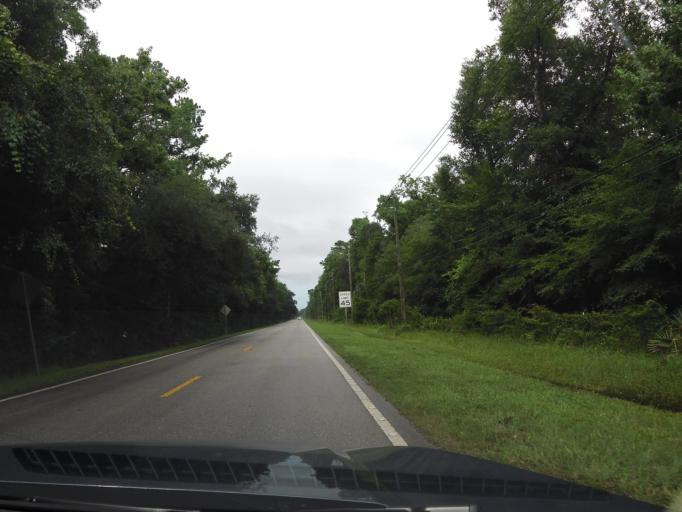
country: US
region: Florida
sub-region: Saint Johns County
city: Saint Augustine South
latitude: 29.8640
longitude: -81.3820
